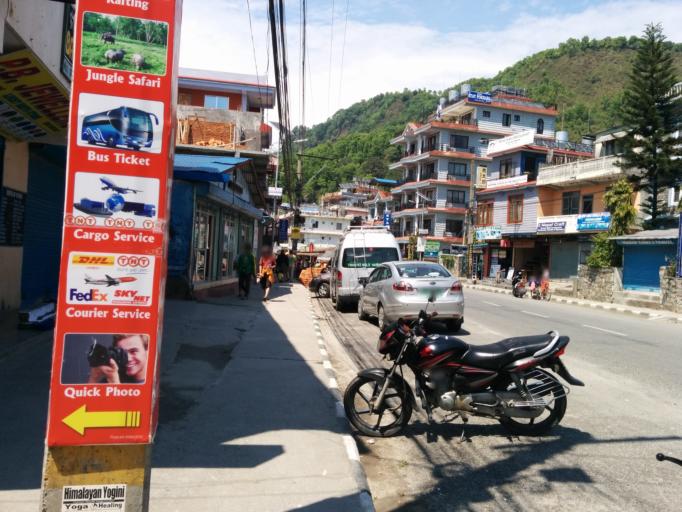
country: NP
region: Western Region
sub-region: Gandaki Zone
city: Pokhara
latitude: 28.2156
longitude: 83.9584
